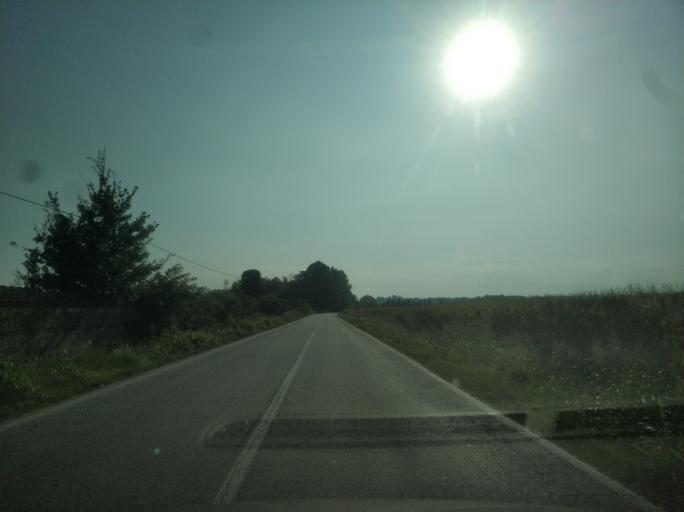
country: IT
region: Piedmont
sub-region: Provincia di Cuneo
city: Bra
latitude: 44.6786
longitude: 7.8784
